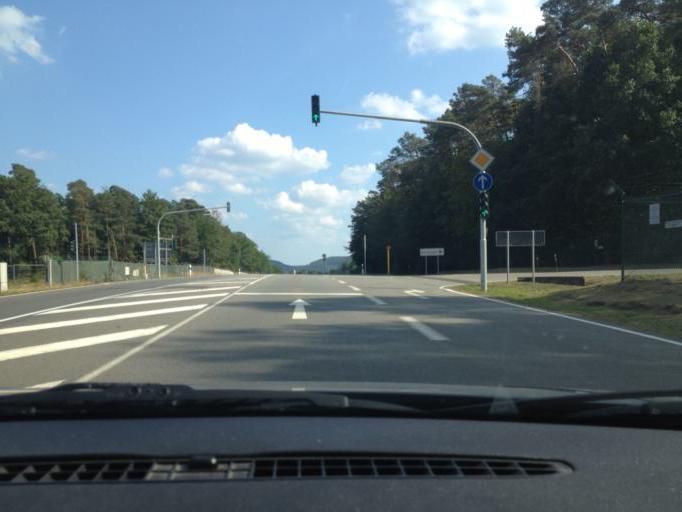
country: DE
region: Rheinland-Pfalz
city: Kindsbach
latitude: 49.4493
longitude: 7.6141
